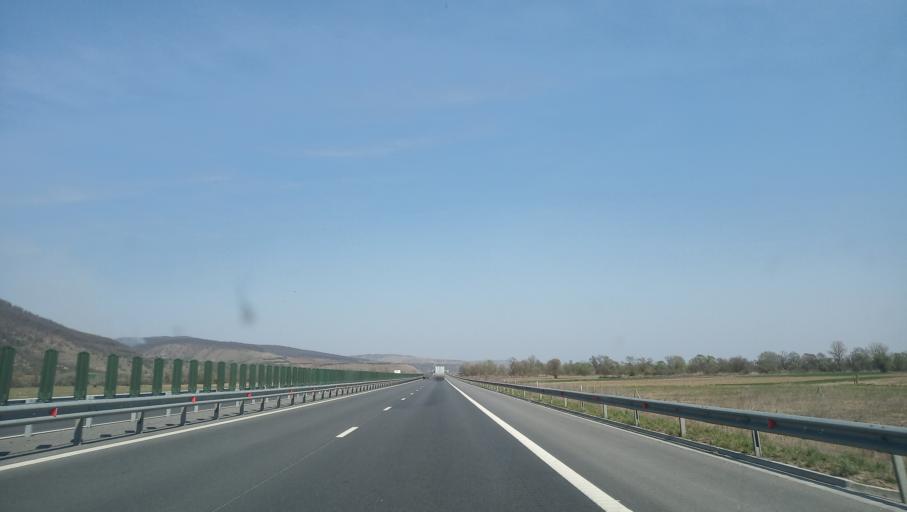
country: RO
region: Alba
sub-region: Comuna Miraslau
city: Miraslau
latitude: 46.3581
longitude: 23.7276
